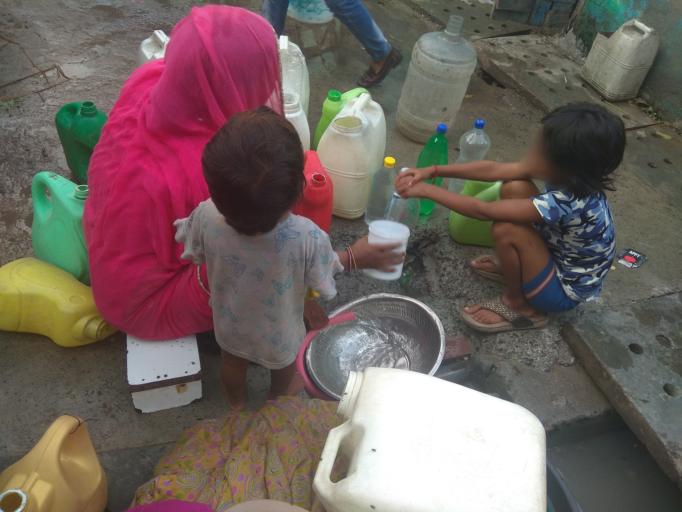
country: IN
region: NCT
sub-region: New Delhi
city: New Delhi
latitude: 28.5695
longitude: 77.2501
